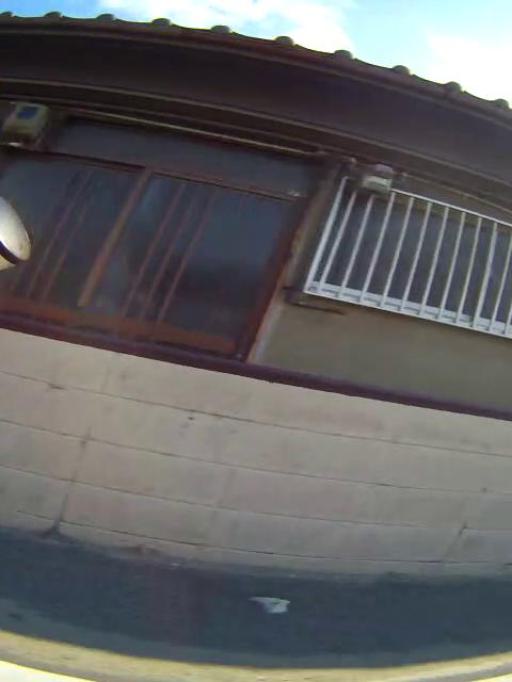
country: JP
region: Osaka
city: Yao
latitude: 34.6450
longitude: 135.6379
